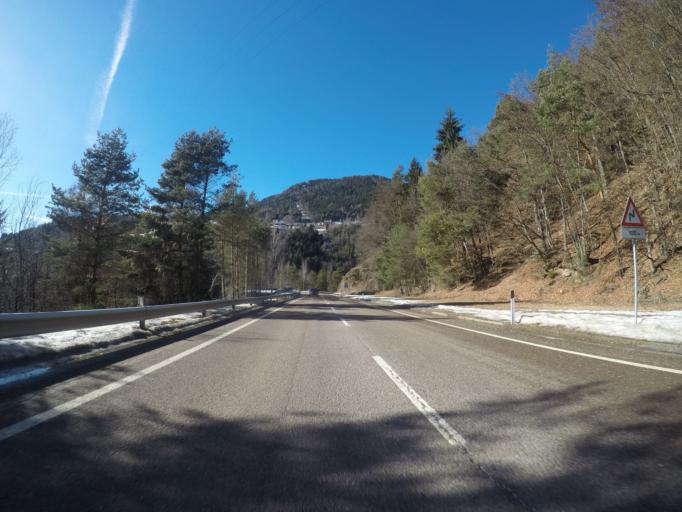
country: IT
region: Trentino-Alto Adige
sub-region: Provincia di Trento
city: Capriana
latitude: 46.2656
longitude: 11.3476
